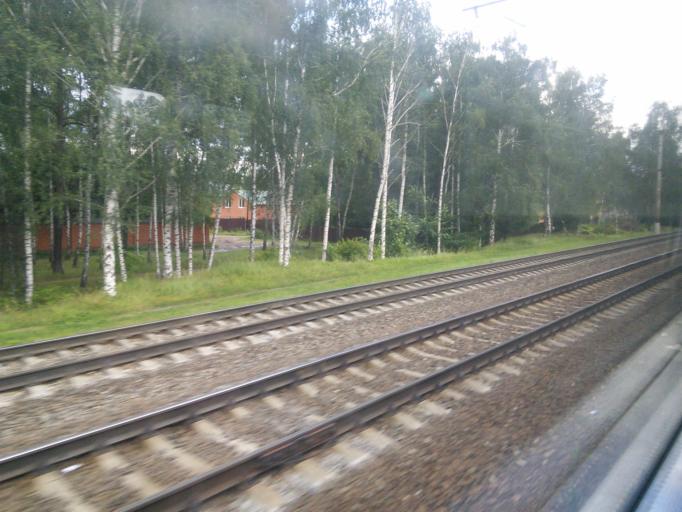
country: RU
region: Moskovskaya
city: Malakhovka
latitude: 55.6399
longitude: 38.0279
